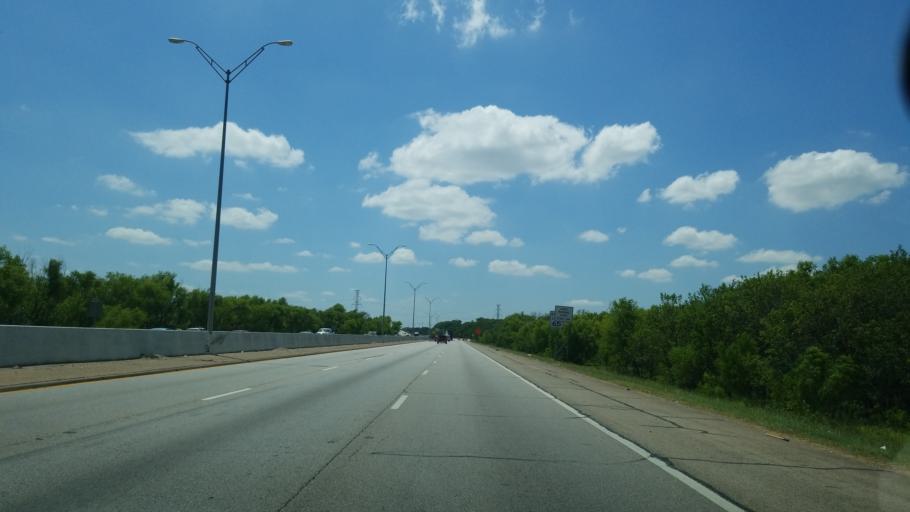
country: US
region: Texas
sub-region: Dallas County
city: Dallas
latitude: 32.7466
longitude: -96.7371
